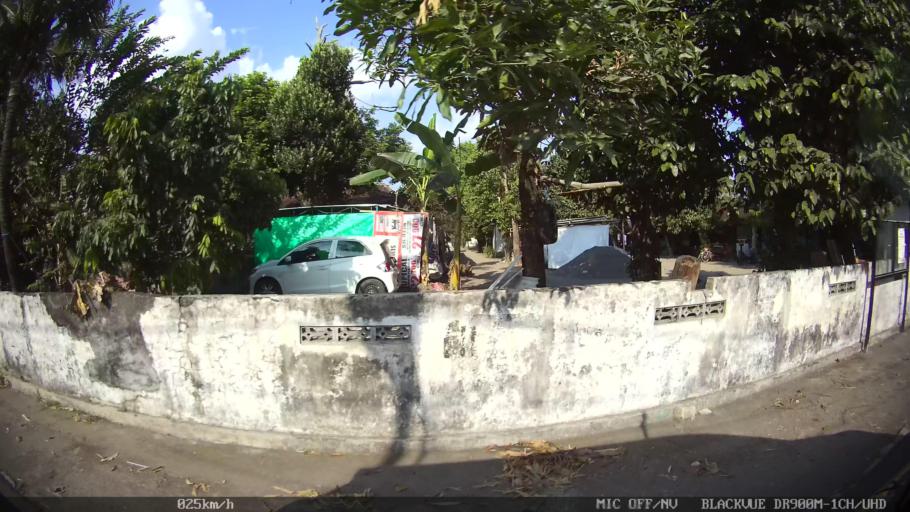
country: ID
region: Daerah Istimewa Yogyakarta
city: Yogyakarta
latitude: -7.8220
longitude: 110.3788
